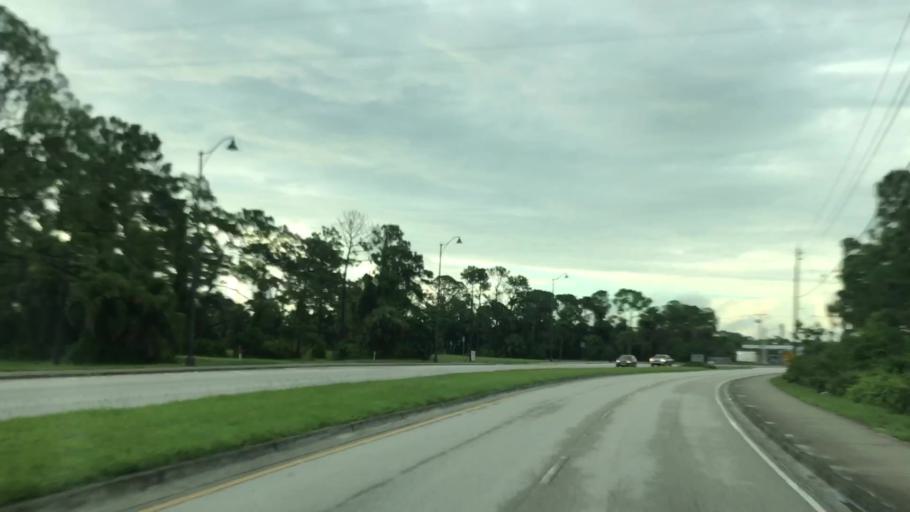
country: US
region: Florida
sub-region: Lee County
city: Bonita Springs
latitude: 26.3530
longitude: -81.7804
